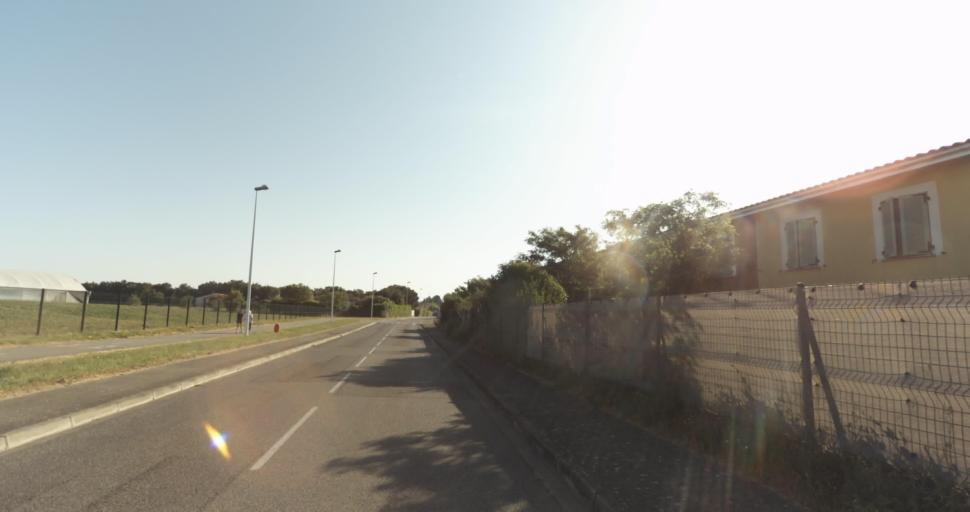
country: FR
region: Midi-Pyrenees
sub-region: Departement de la Haute-Garonne
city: La Salvetat-Saint-Gilles
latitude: 43.5708
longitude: 1.2477
